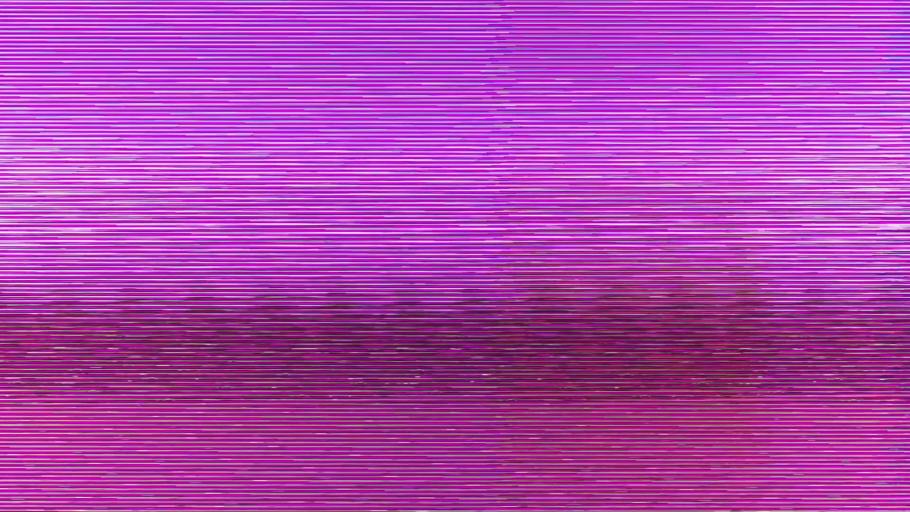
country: US
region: Michigan
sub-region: Oakland County
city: Oxford
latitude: 42.8554
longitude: -83.2850
